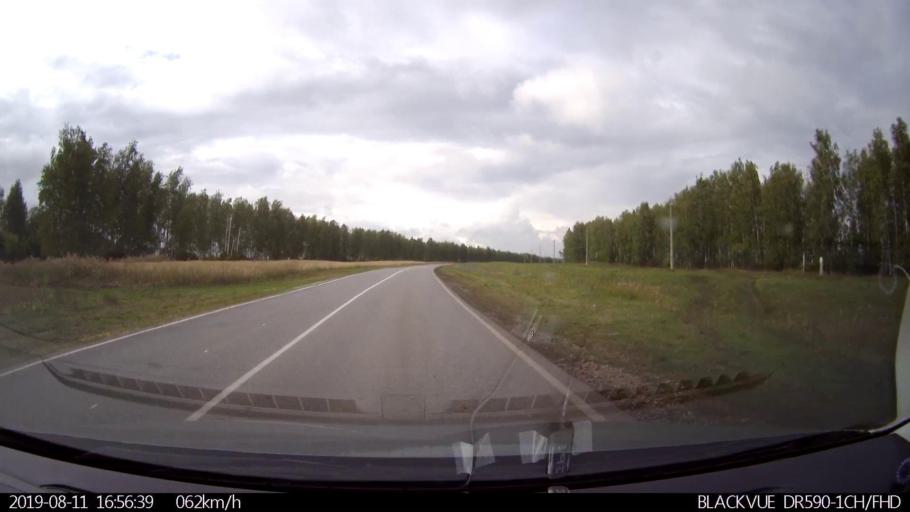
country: RU
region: Ulyanovsk
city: Mayna
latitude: 54.2889
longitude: 47.6524
